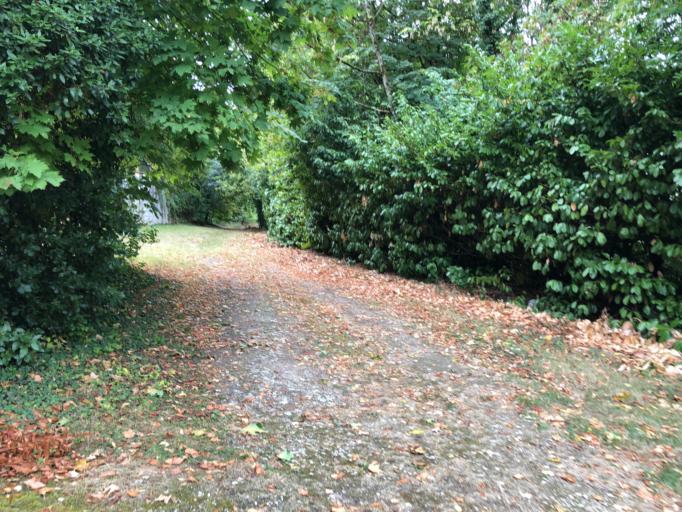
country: FR
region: Centre
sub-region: Departement du Loir-et-Cher
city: Saint-Gervais-la-Foret
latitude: 47.5701
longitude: 1.3526
